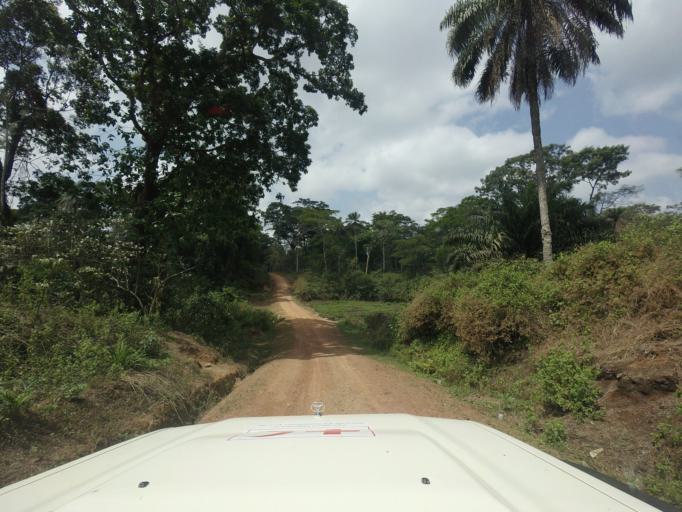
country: LR
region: Lofa
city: Voinjama
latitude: 8.4598
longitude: -9.6368
